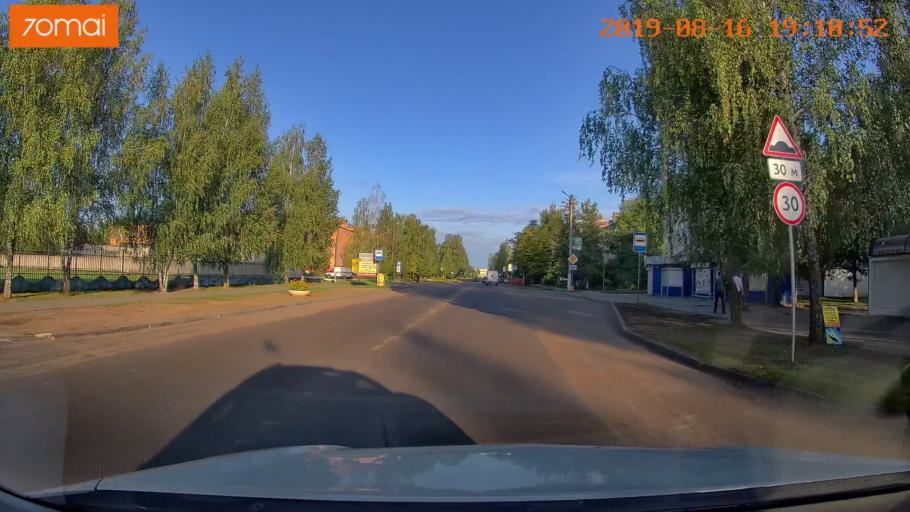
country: BY
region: Mogilev
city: Asipovichy
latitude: 53.3227
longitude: 28.6445
